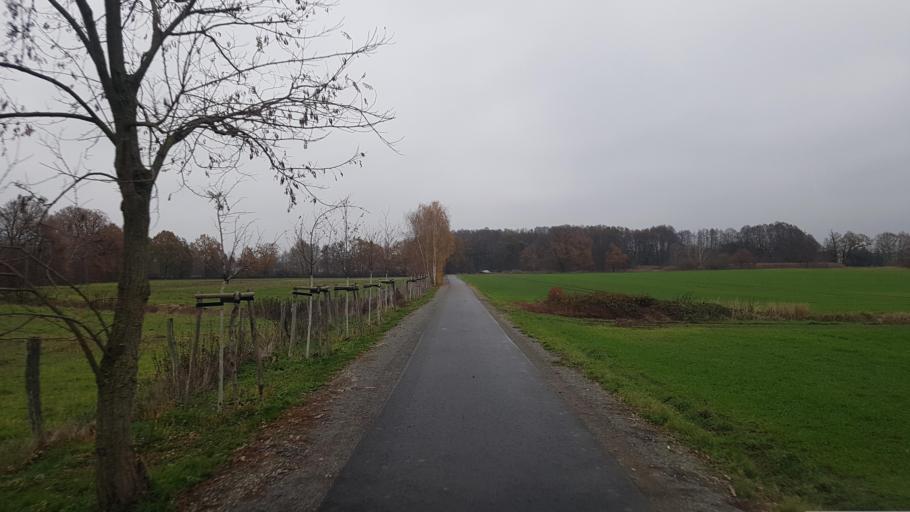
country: DE
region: Brandenburg
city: Crinitz
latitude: 51.7583
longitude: 13.7964
